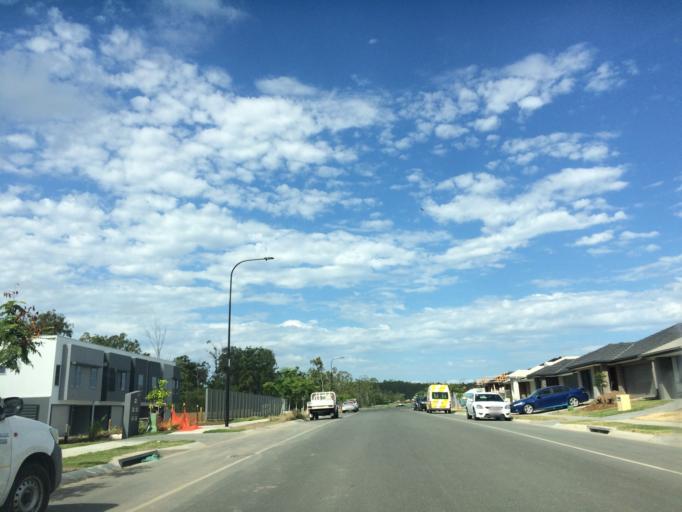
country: AU
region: Queensland
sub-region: Logan
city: North Maclean
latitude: -27.8022
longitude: 152.9430
